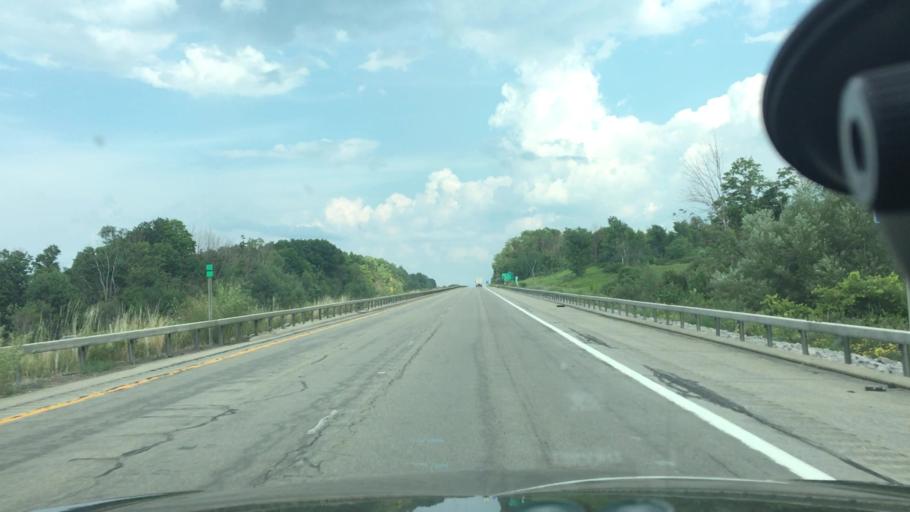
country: US
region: New York
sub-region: Cattaraugus County
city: Randolph
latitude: 42.1623
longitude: -79.0220
